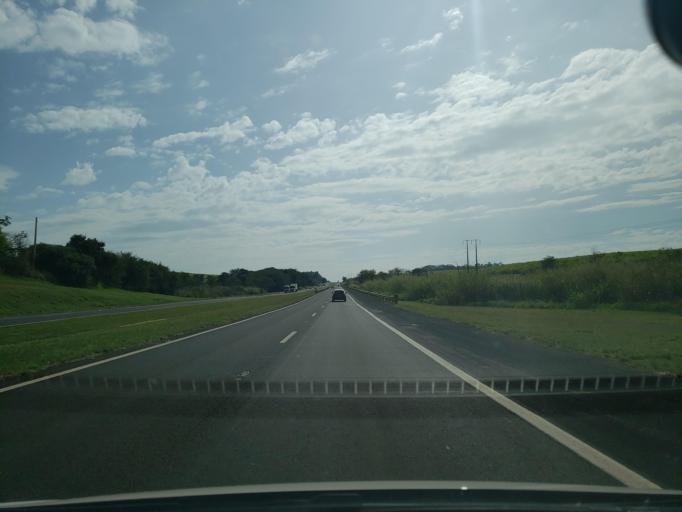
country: BR
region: Sao Paulo
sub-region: Lins
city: Lins
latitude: -21.7312
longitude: -49.7103
